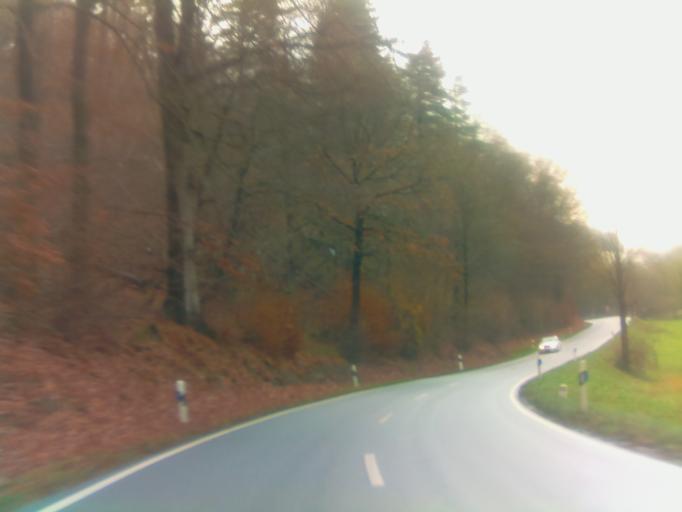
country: DE
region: Hesse
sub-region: Regierungsbezirk Darmstadt
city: Wald-Michelbach
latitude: 49.5742
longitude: 8.7886
